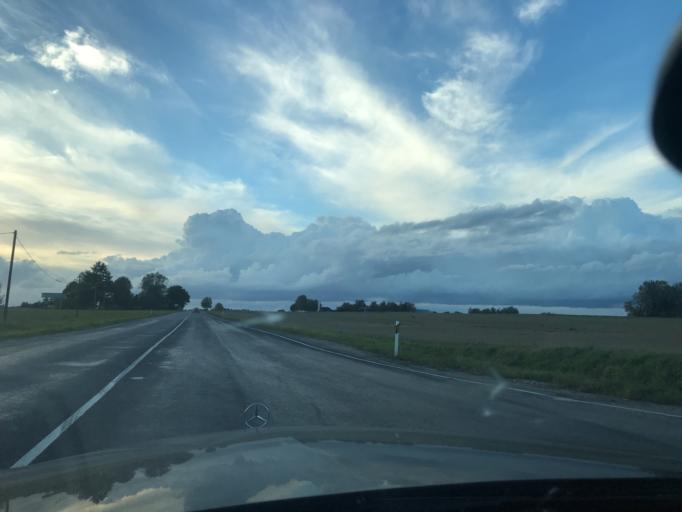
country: EE
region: Vorumaa
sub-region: Antsla vald
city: Vana-Antsla
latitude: 57.8849
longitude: 26.5265
